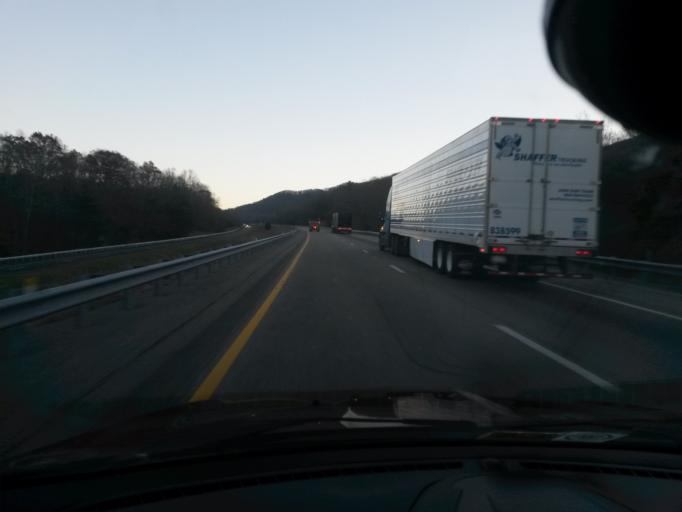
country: US
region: Virginia
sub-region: Alleghany County
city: Clifton Forge
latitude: 37.8393
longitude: -79.6428
